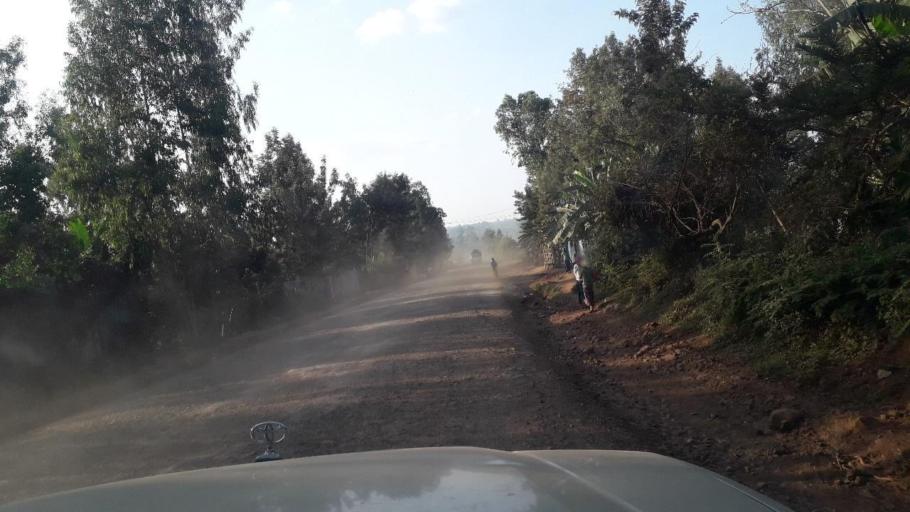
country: ET
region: Oromiya
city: Jima
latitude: 7.6078
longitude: 36.8381
